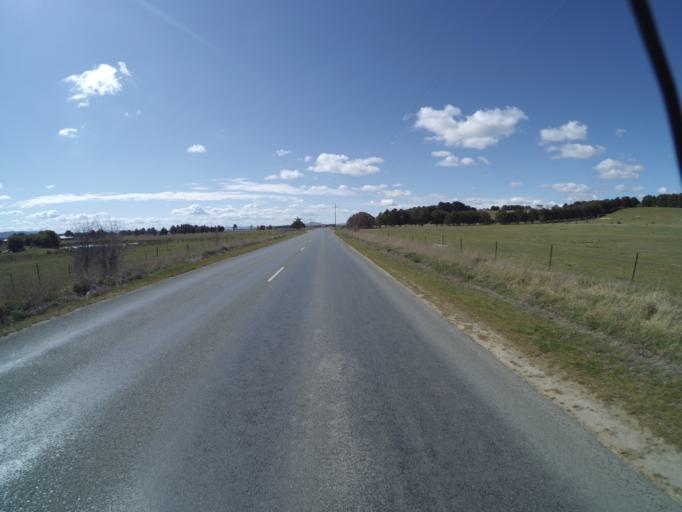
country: AU
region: New South Wales
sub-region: Palerang
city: Bungendore
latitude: -35.2344
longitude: 149.4453
